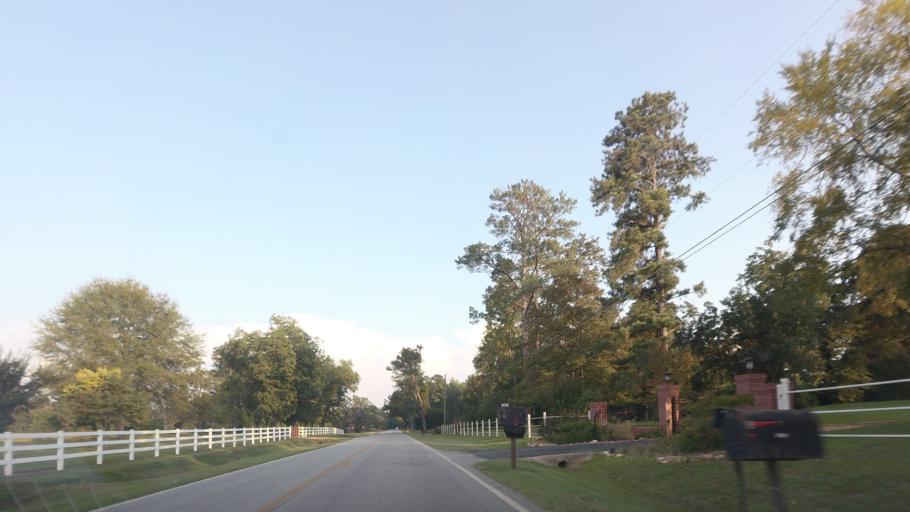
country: US
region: Georgia
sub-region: Bibb County
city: West Point
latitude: 32.8893
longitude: -83.7983
